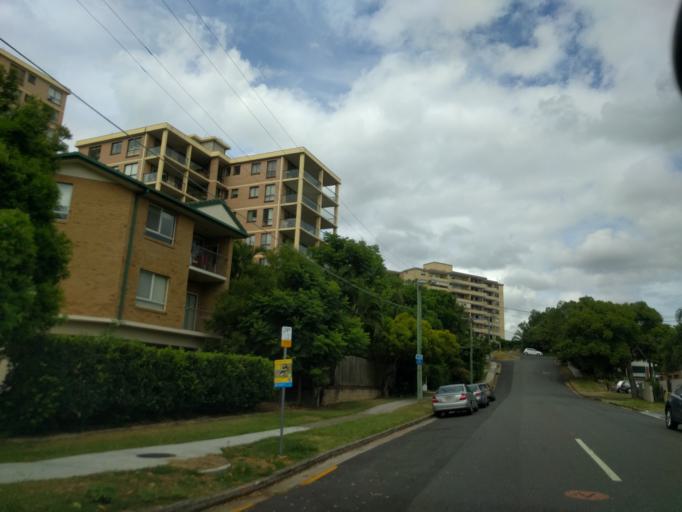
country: AU
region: Queensland
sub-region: Brisbane
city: Toowong
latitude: -27.4930
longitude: 153.0002
